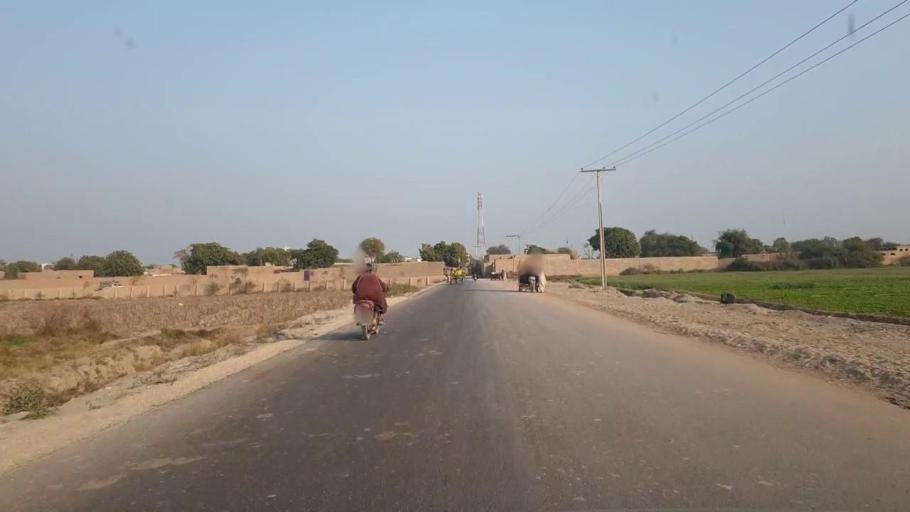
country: PK
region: Sindh
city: Bhit Shah
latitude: 25.8070
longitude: 68.4826
